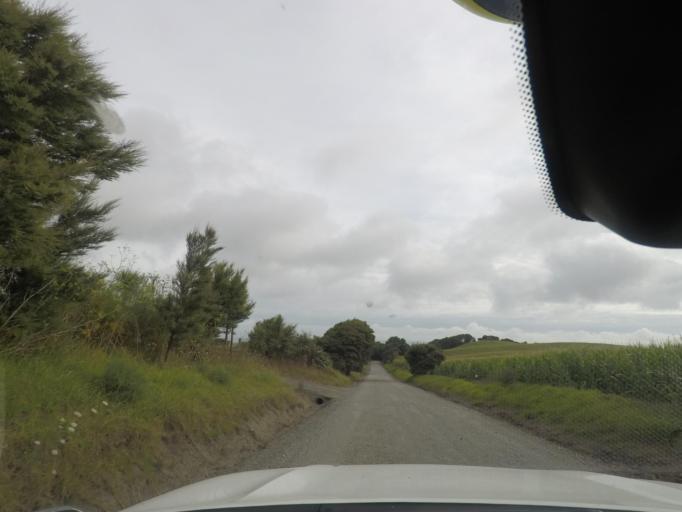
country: NZ
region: Auckland
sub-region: Auckland
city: Parakai
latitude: -36.4807
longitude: 174.2544
